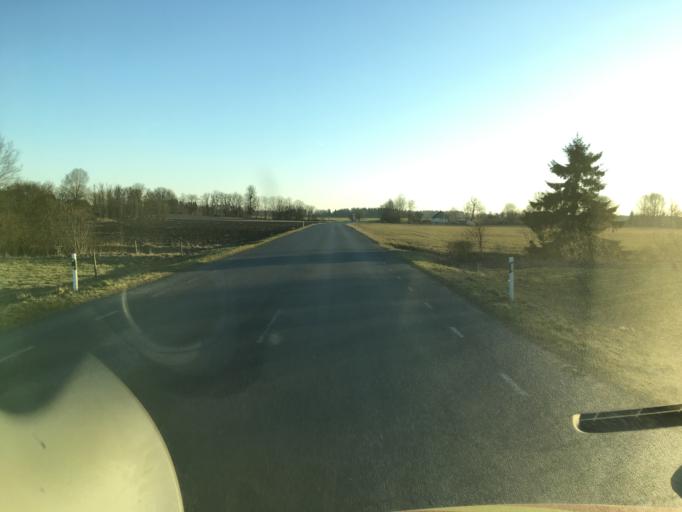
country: EE
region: Raplamaa
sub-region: Kehtna vald
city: Kehtna
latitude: 59.0083
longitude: 24.9090
